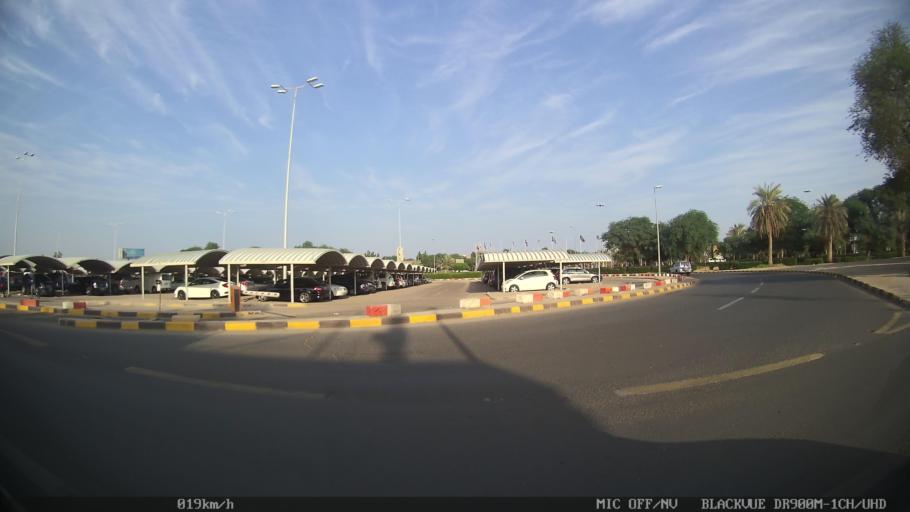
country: KW
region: Al Farwaniyah
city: Janub as Surrah
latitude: 29.2454
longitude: 47.9665
